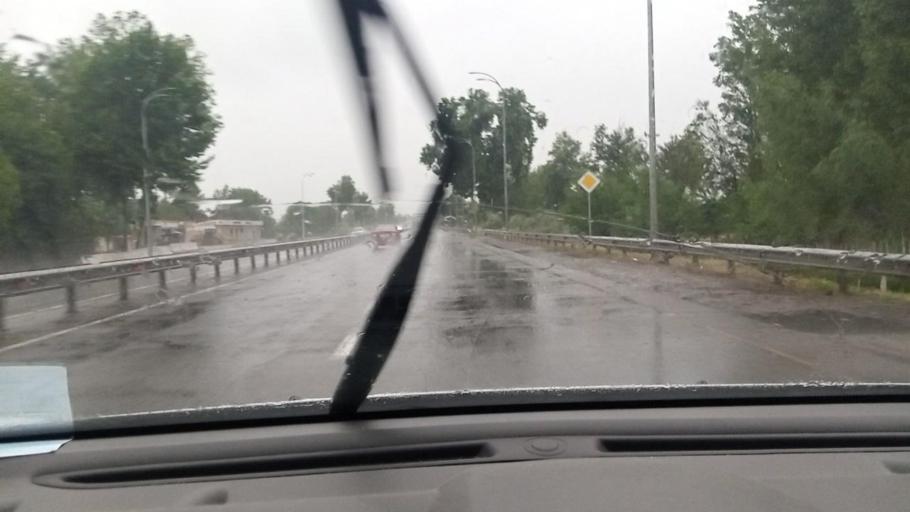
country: UZ
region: Toshkent Shahri
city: Bektemir
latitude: 41.2529
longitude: 69.3856
